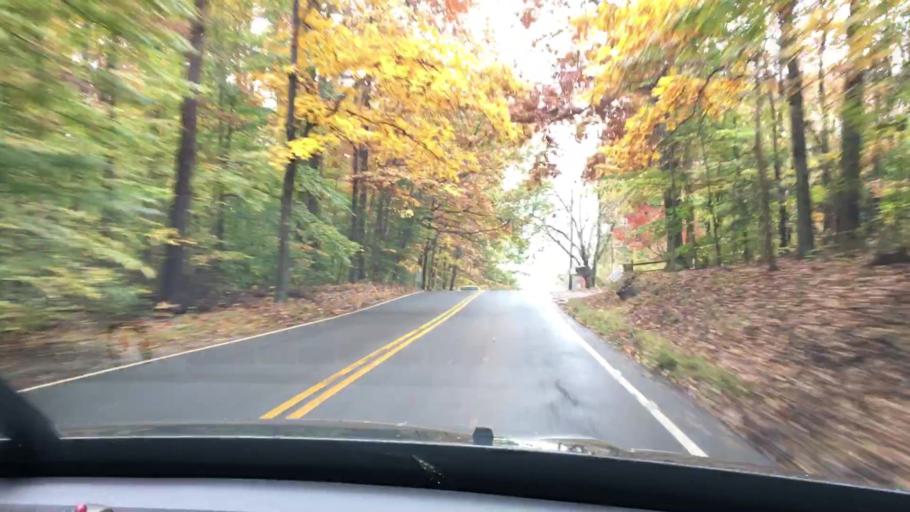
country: US
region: Virginia
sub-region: Fairfax County
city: Burke
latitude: 38.7507
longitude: -77.2800
